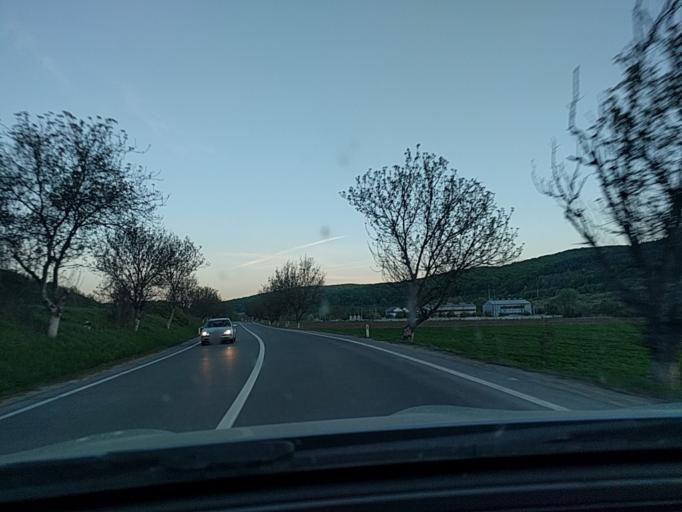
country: RO
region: Mures
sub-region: Comuna Nades
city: Nades
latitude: 46.3342
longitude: 24.7105
